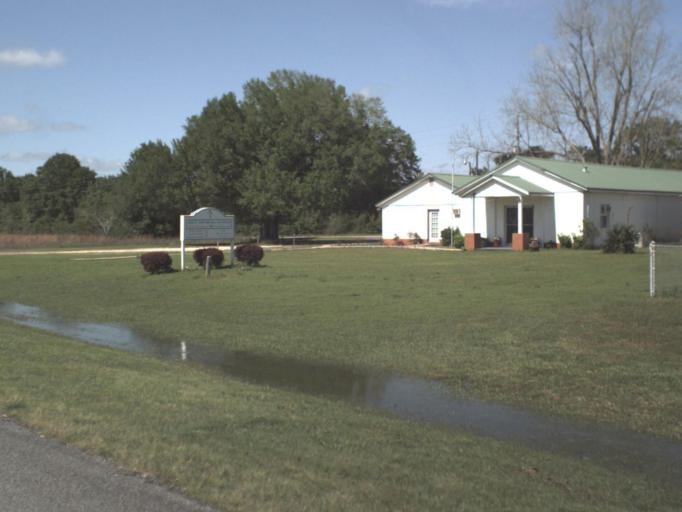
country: US
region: Florida
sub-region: Escambia County
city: Cantonment
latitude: 30.6017
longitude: -87.3146
